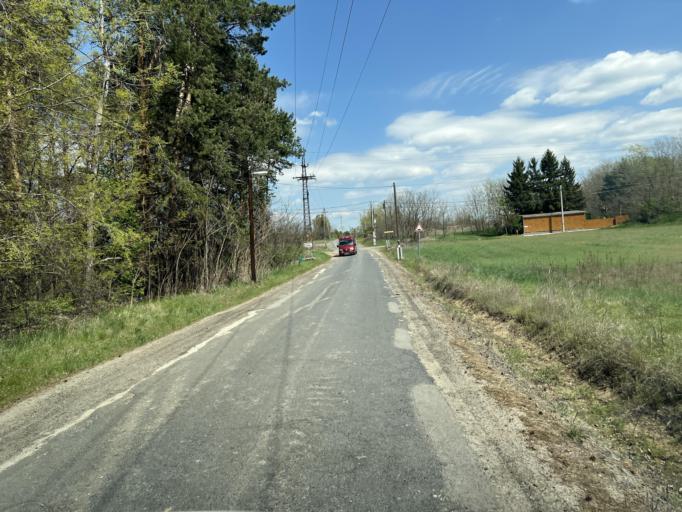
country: HU
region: Pest
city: Inarcs
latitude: 47.2589
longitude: 19.3394
